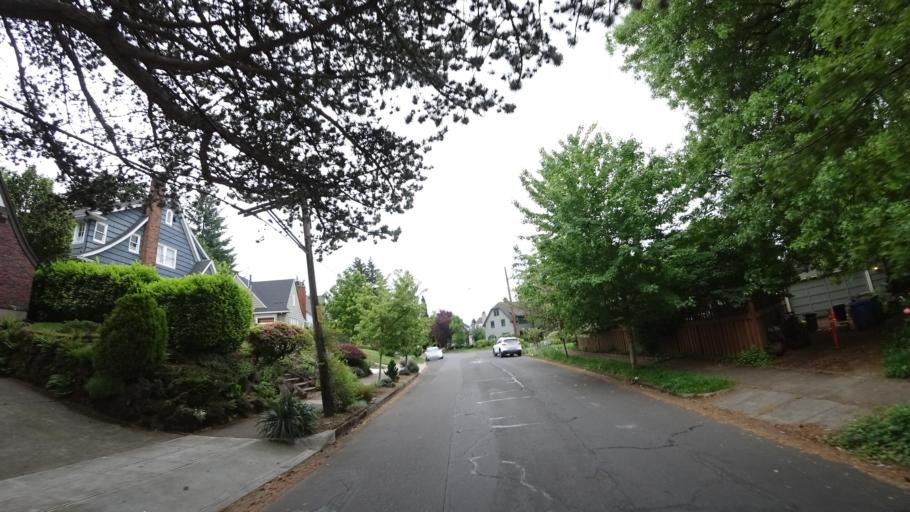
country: US
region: Oregon
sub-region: Multnomah County
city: Portland
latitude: 45.5423
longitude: -122.6184
